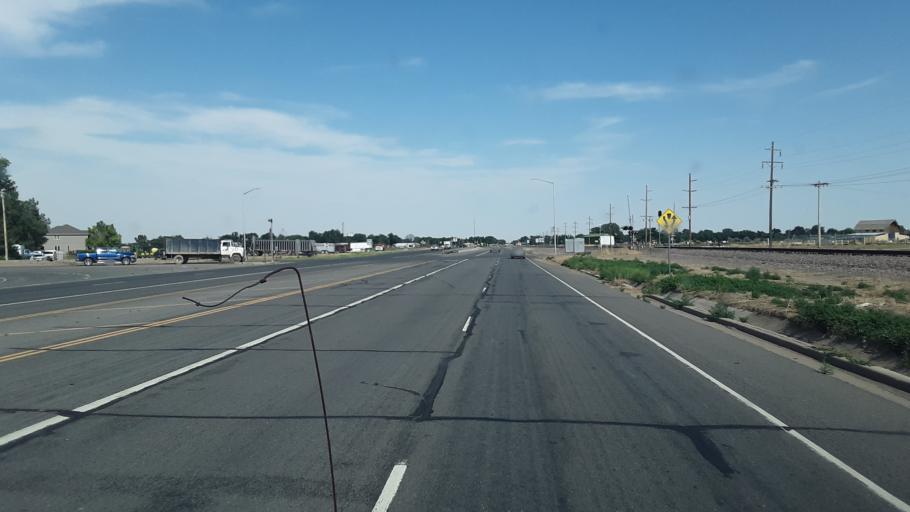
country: US
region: Colorado
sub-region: Otero County
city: Rocky Ford
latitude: 38.0646
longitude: -103.7488
